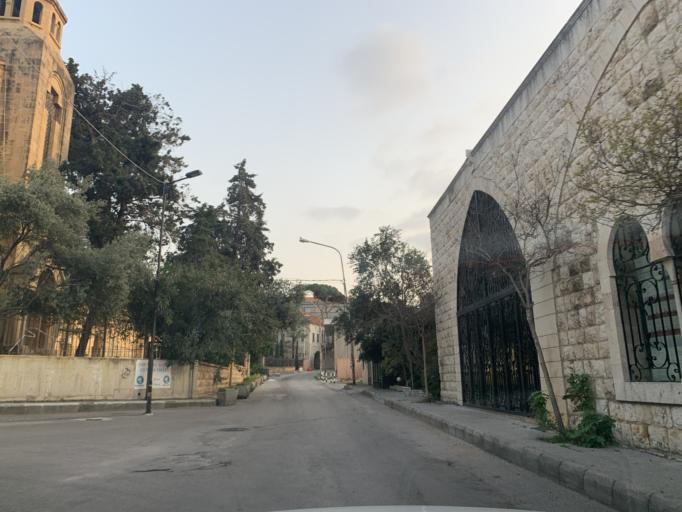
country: LB
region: Mont-Liban
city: Djounie
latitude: 33.9823
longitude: 35.6319
